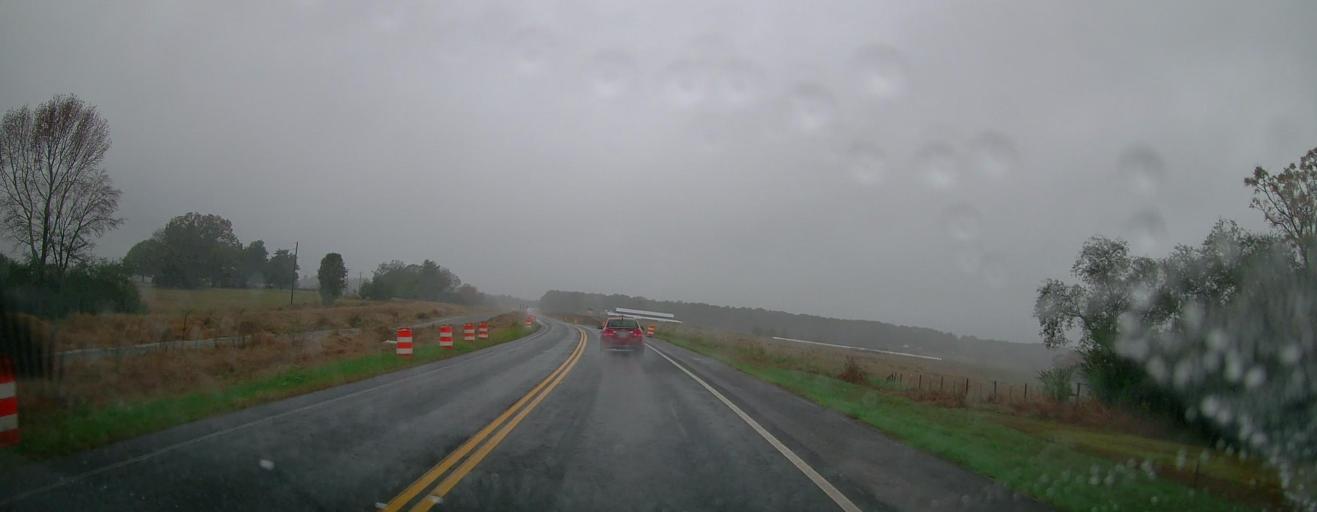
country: US
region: Georgia
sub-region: Putnam County
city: Jefferson
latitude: 33.4712
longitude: -83.4185
